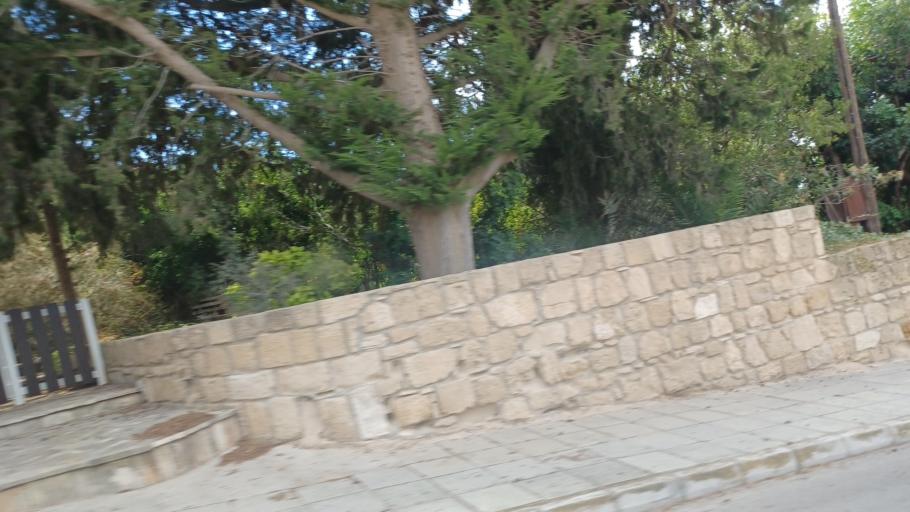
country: CY
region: Pafos
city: Mesogi
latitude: 34.8108
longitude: 32.4635
